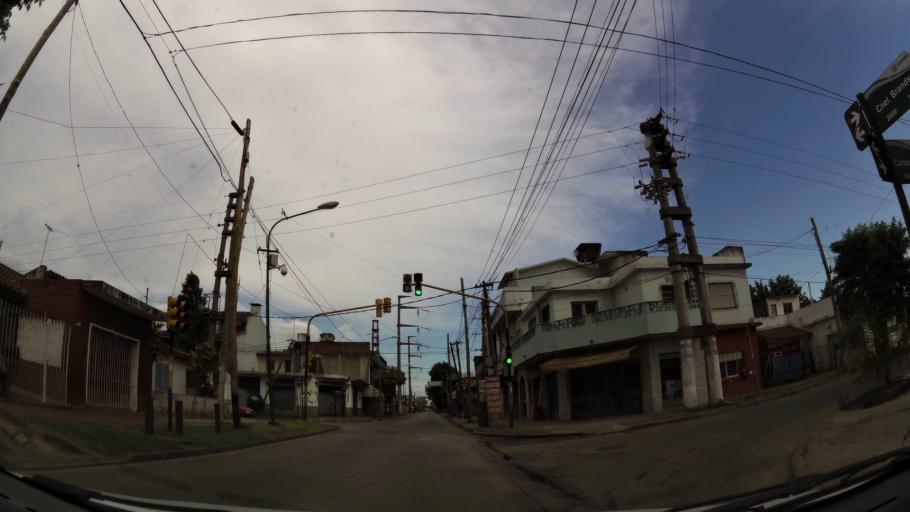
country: AR
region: Buenos Aires
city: Ituzaingo
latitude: -34.6389
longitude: -58.6907
